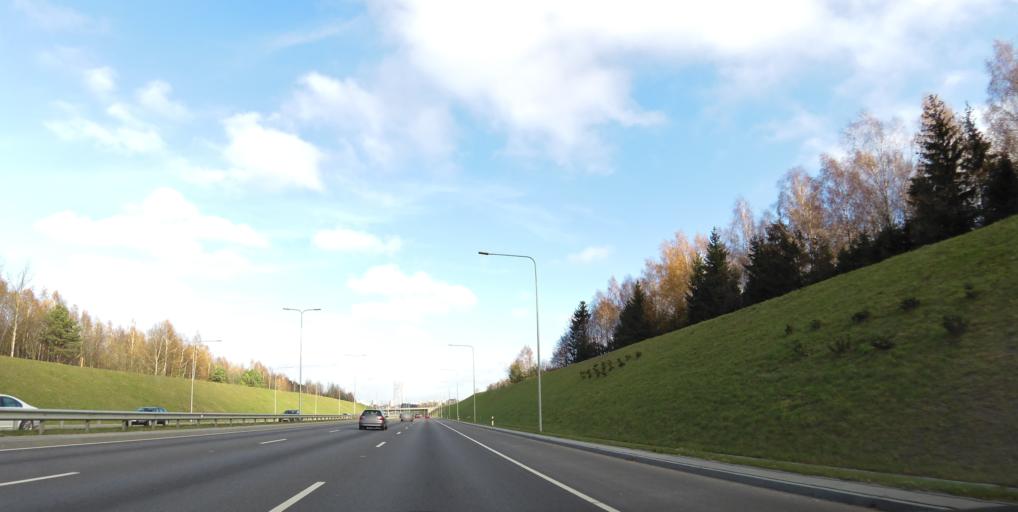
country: LT
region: Vilnius County
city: Pilaite
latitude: 54.6911
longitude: 25.2014
